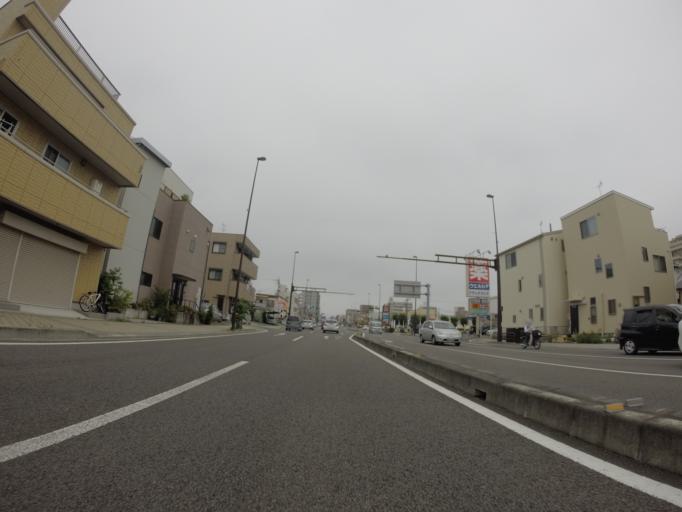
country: JP
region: Shizuoka
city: Shizuoka-shi
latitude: 34.9621
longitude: 138.3934
